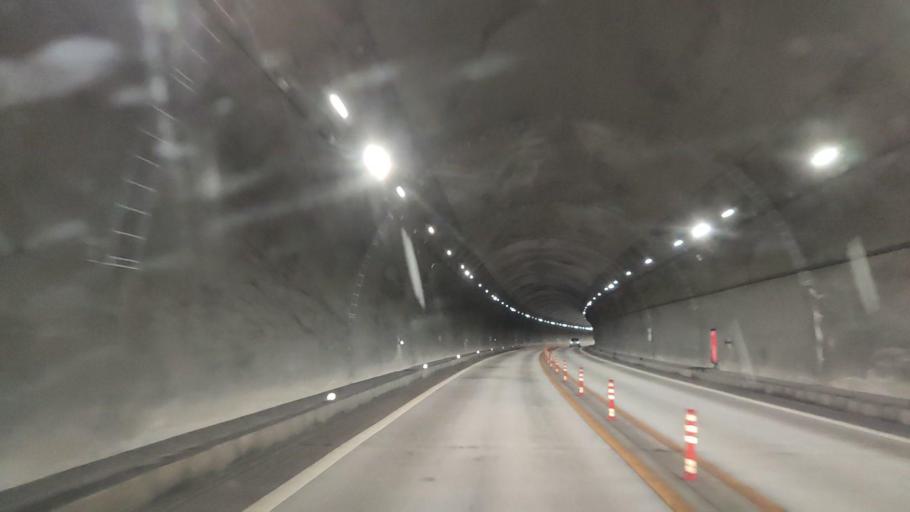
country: JP
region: Hiroshima
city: Innoshima
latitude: 34.1307
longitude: 133.0234
